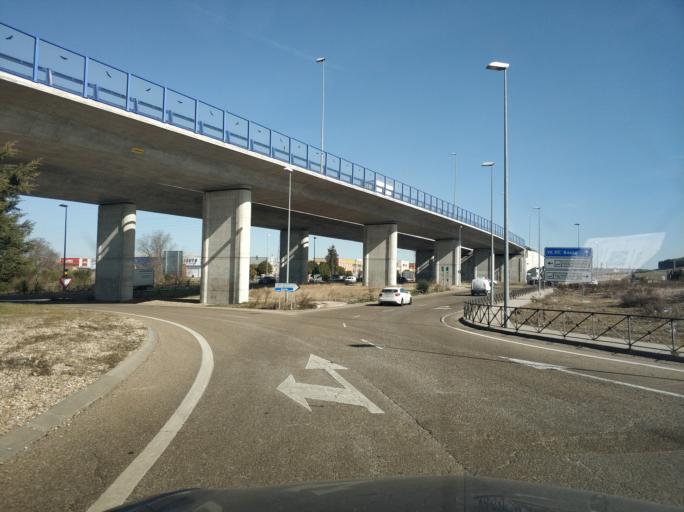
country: ES
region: Castille and Leon
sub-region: Provincia de Valladolid
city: Cisterniga
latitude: 41.6124
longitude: -4.7125
